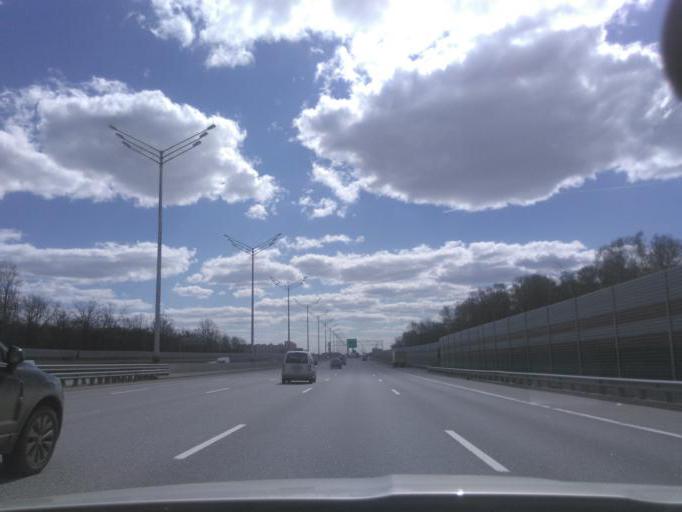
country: RU
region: Moscow
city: Khimki
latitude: 55.9146
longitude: 37.4623
